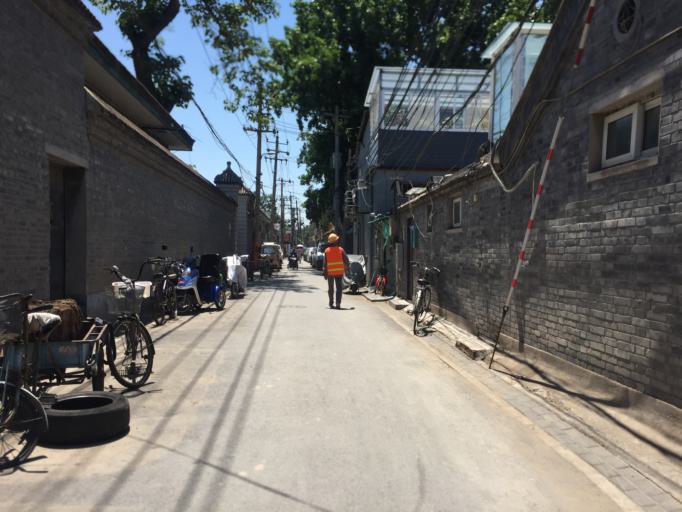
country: CN
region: Beijing
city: Jingshan
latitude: 39.9311
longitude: 116.3874
